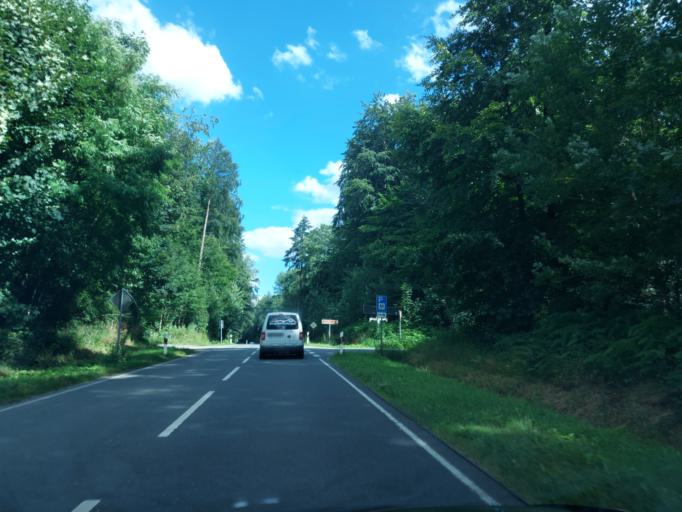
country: DE
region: Lower Saxony
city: Bad Iburg
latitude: 52.1752
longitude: 8.0232
